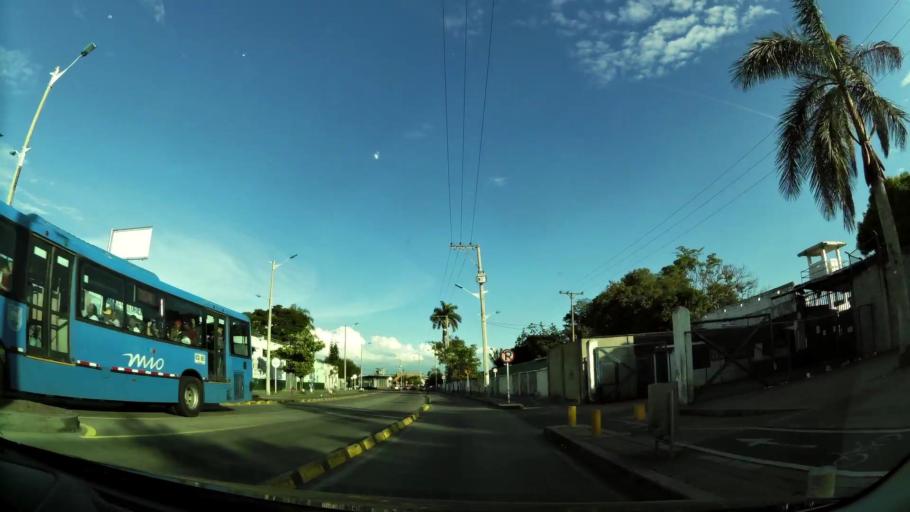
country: CO
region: Valle del Cauca
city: Cali
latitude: 3.4327
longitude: -76.5115
